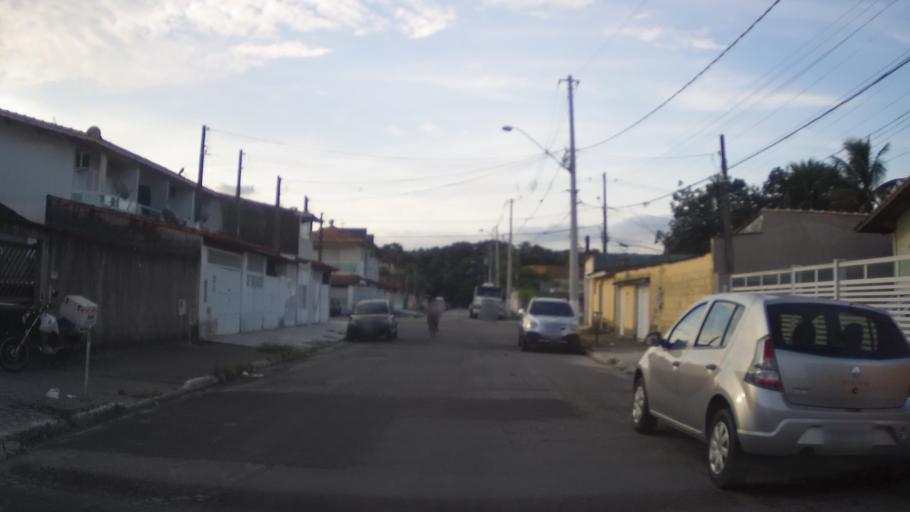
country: BR
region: Sao Paulo
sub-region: Praia Grande
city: Praia Grande
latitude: -23.9942
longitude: -46.4177
